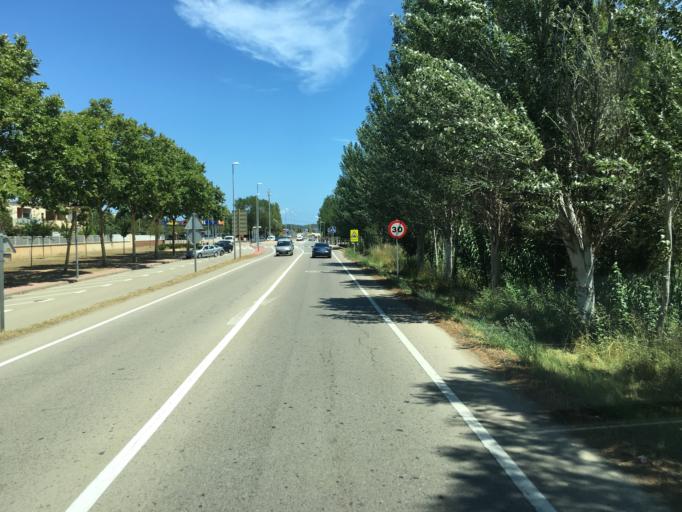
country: ES
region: Catalonia
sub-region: Provincia de Girona
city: Palamos
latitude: 41.8538
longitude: 3.1177
